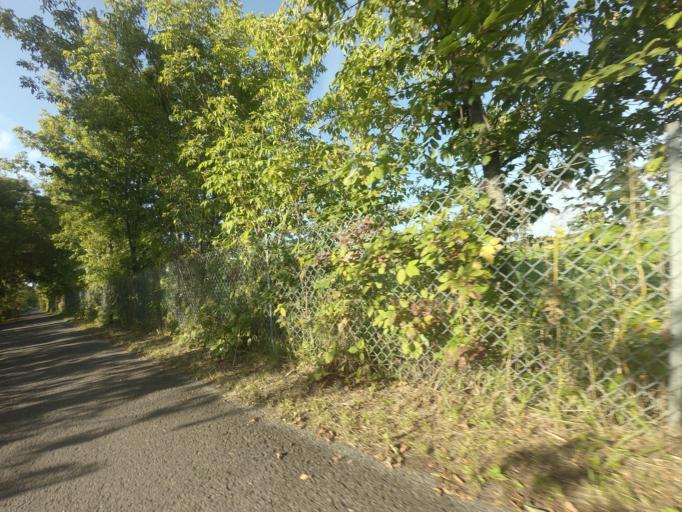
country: CA
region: Quebec
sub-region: Laurentides
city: Saint-Jerome
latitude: 45.7334
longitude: -73.9472
